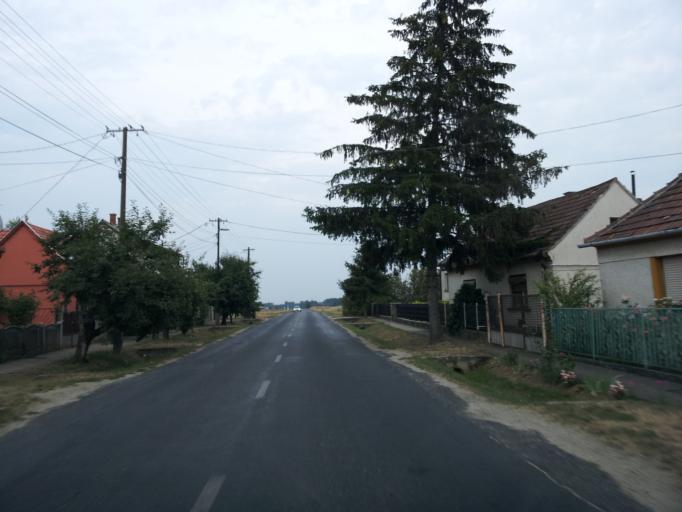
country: HU
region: Vas
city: Vep
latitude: 47.2044
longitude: 16.7939
